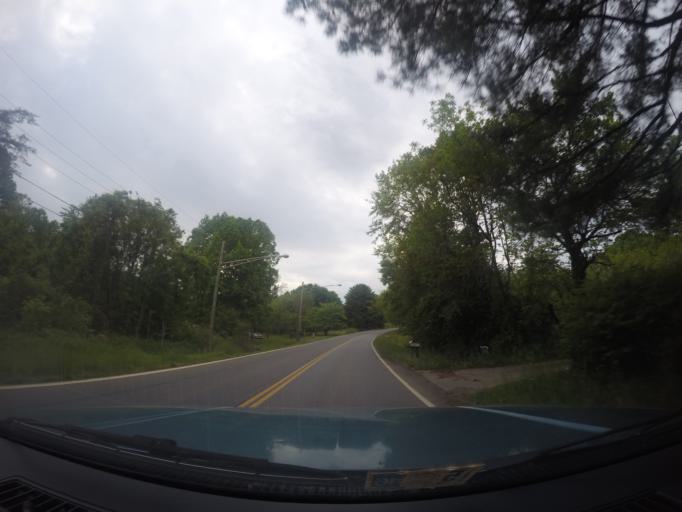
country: US
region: Virginia
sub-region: Amherst County
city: Madison Heights
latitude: 37.3896
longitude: -79.1021
